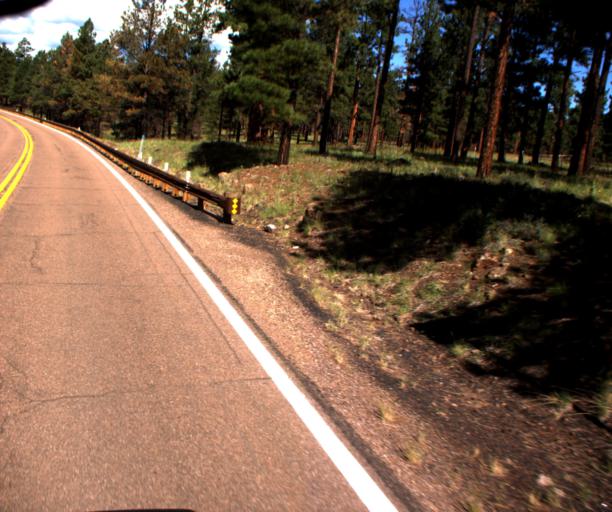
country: US
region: Arizona
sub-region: Apache County
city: Eagar
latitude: 34.0770
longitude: -109.4707
